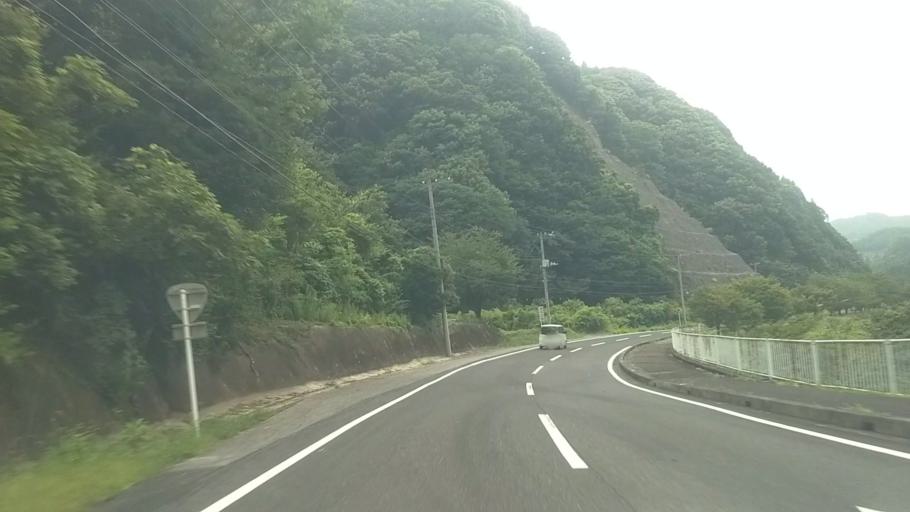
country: JP
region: Chiba
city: Kawaguchi
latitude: 35.2350
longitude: 140.1612
